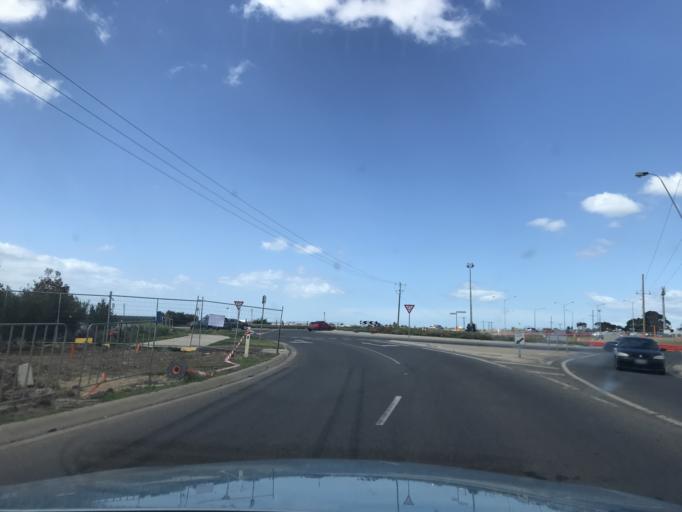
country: AU
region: Victoria
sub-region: Wyndham
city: Williams Landing
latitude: -37.8668
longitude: 144.7342
